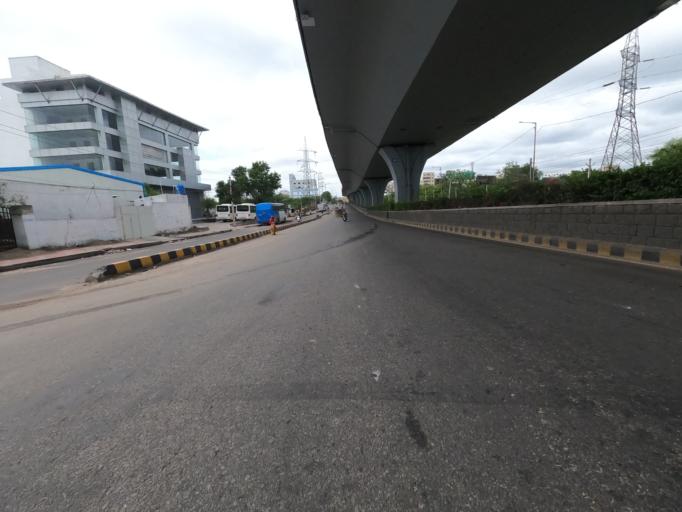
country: IN
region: Telangana
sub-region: Hyderabad
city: Hyderabad
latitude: 17.3403
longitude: 78.4245
